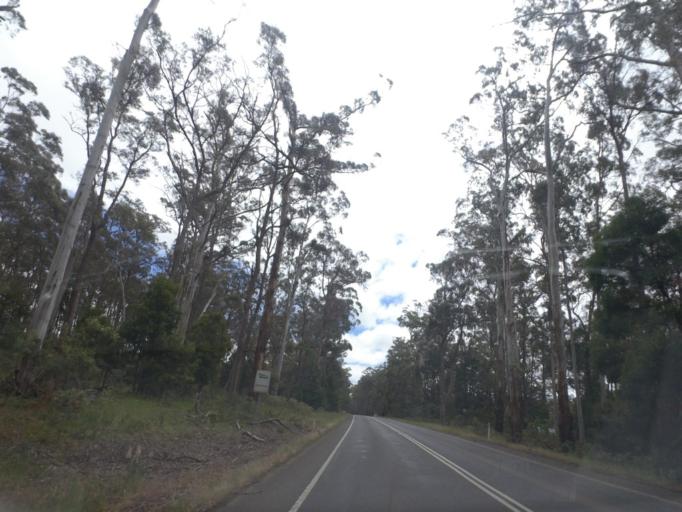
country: AU
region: Victoria
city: Brown Hill
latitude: -37.4750
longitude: 144.1487
